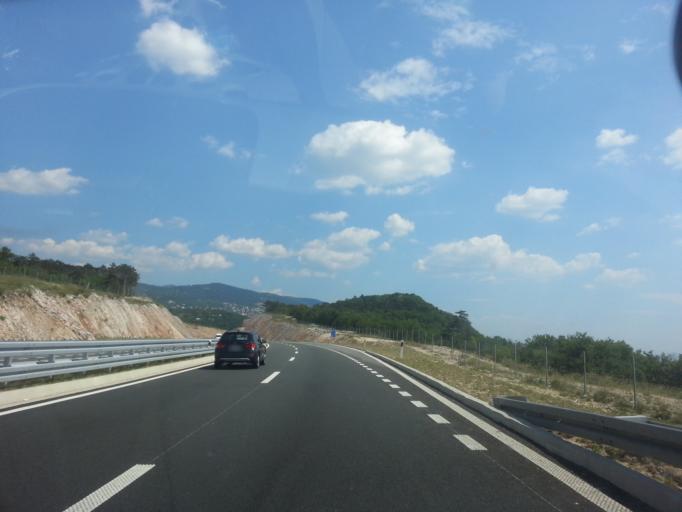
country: HR
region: Primorsko-Goranska
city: Krasica
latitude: 45.2997
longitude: 14.5631
